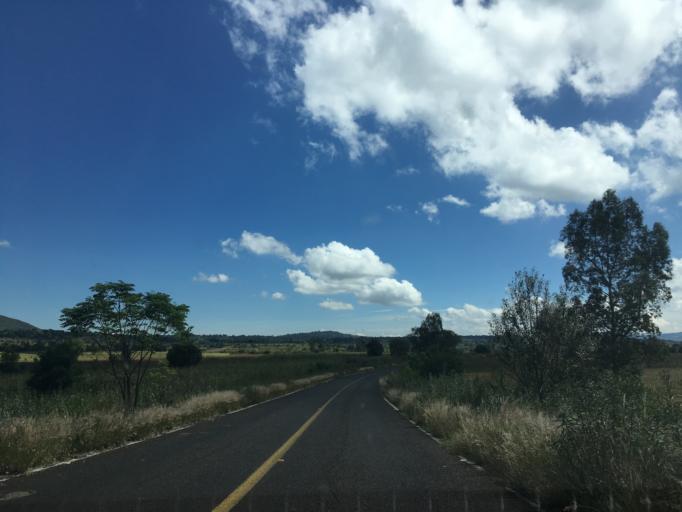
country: MX
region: Michoacan
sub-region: Morelia
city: Cuto de la Esperanza
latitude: 19.7818
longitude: -101.4094
